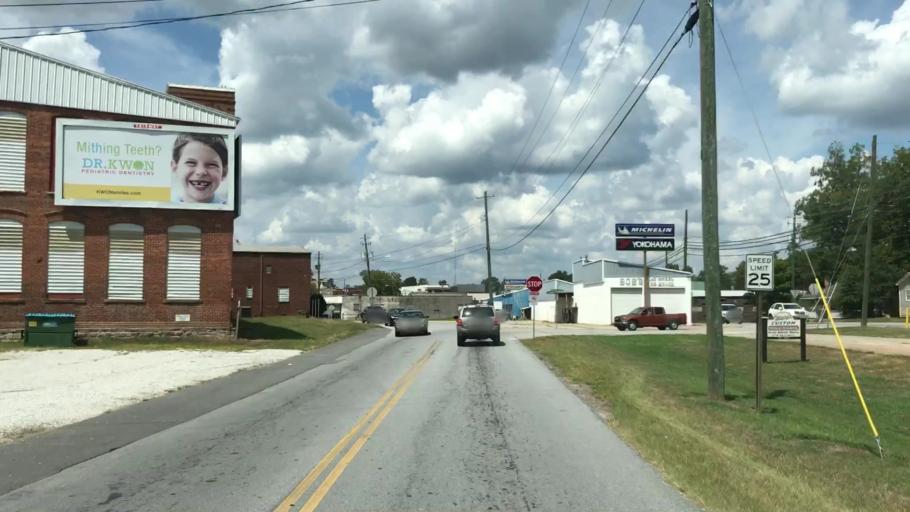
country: US
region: Georgia
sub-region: Barrow County
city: Winder
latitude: 33.9886
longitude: -83.7158
